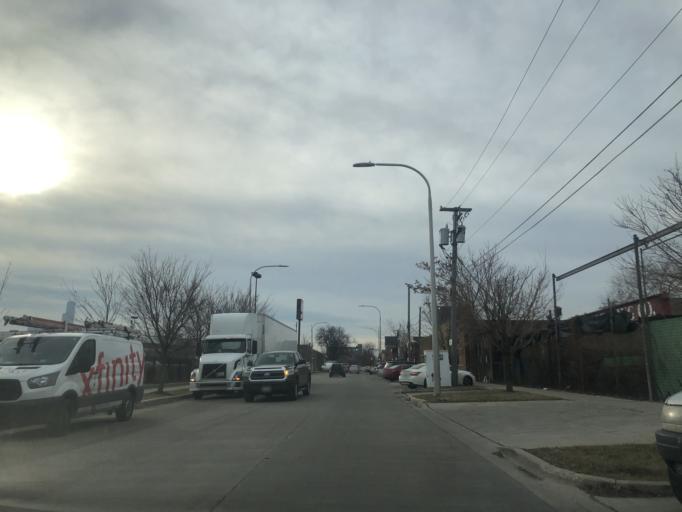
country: US
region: Illinois
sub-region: Cook County
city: Chicago
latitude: 41.9121
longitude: -87.6605
